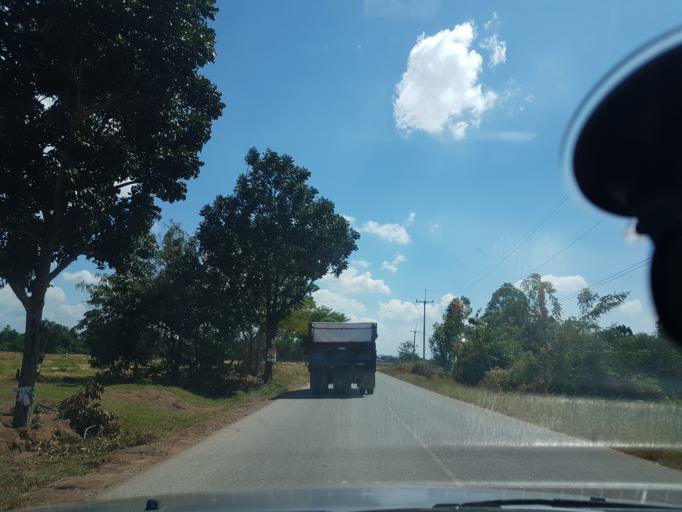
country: TH
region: Lop Buri
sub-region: Amphoe Tha Luang
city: Tha Luang
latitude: 14.9929
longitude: 101.0111
